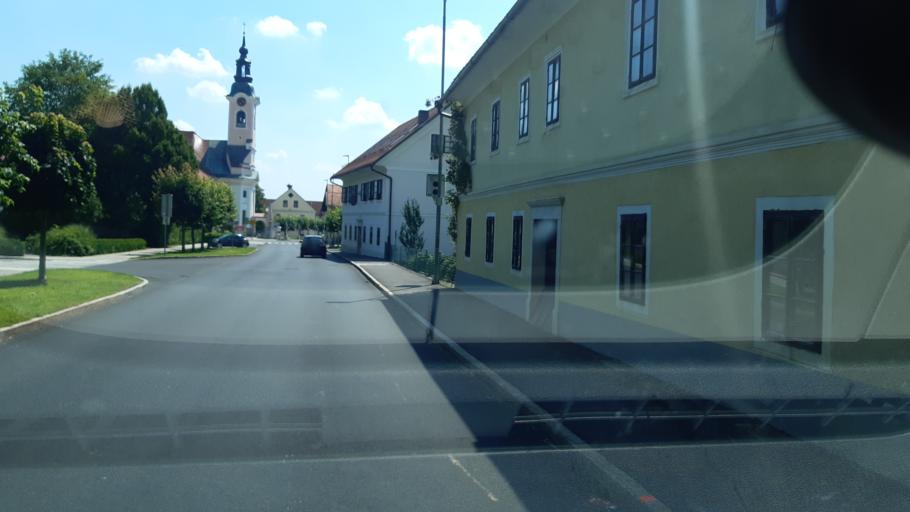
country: SI
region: Cerklje na Gorenjskem
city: Cerklje na Gorenjskem
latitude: 46.2545
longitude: 14.4874
